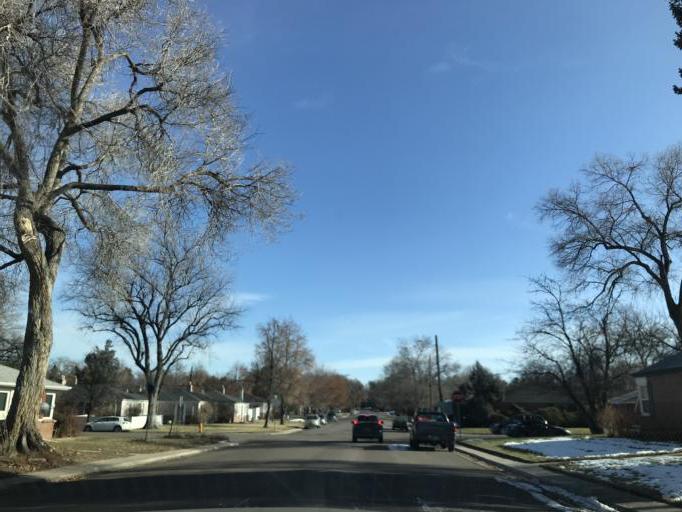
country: US
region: Colorado
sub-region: Arapahoe County
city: Glendale
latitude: 39.7351
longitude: -104.9168
